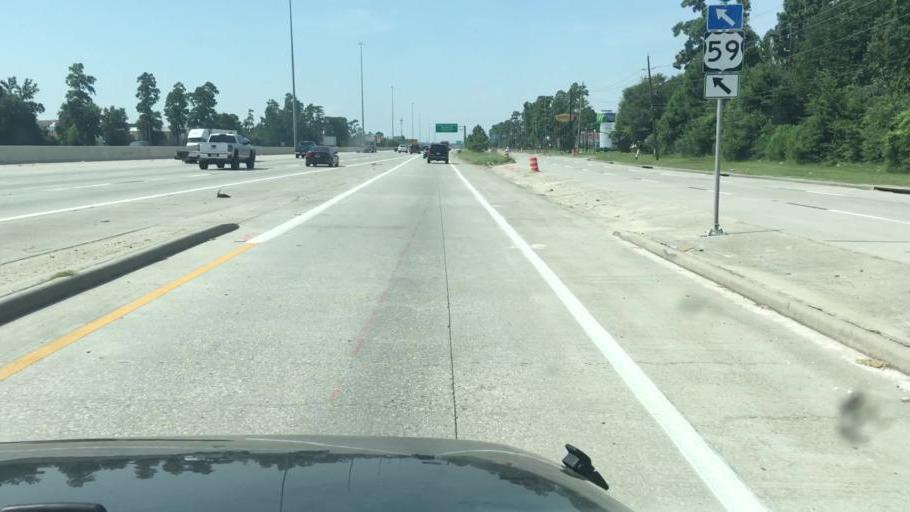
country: US
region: Texas
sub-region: Harris County
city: Humble
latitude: 30.0488
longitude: -95.2553
